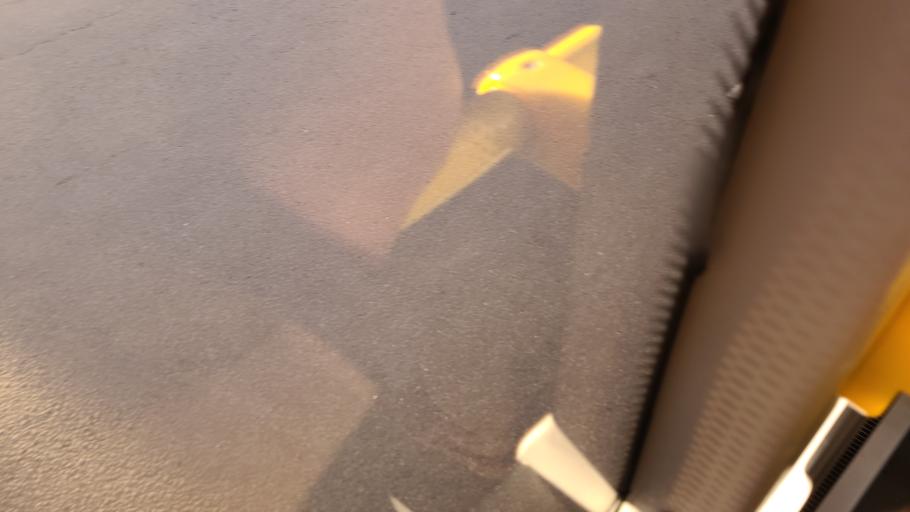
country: RU
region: St.-Petersburg
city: Kolpino
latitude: 59.7410
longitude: 30.5810
